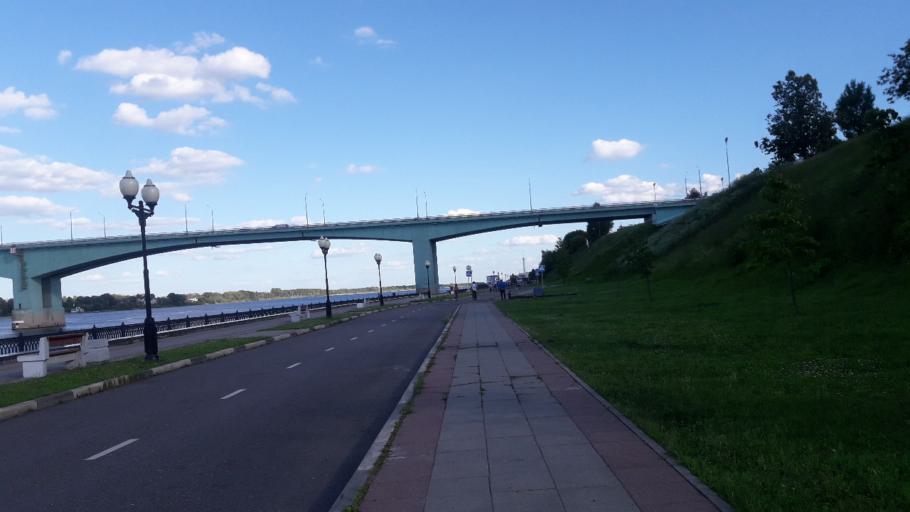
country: RU
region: Jaroslavl
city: Yaroslavl
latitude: 57.6414
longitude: 39.8871
